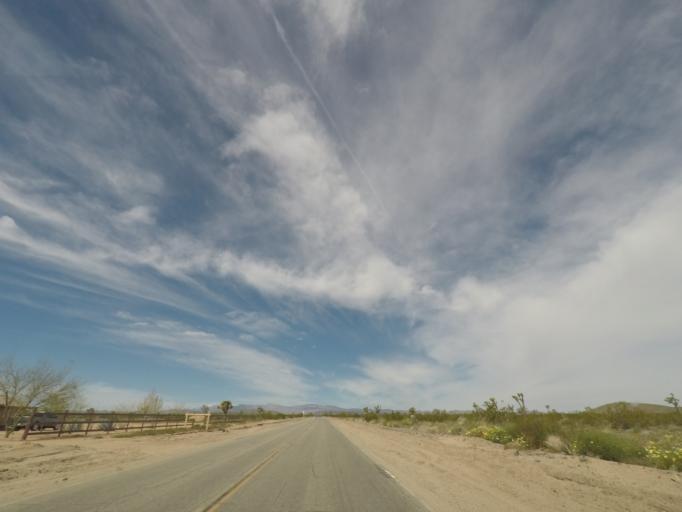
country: US
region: California
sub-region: San Bernardino County
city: Joshua Tree
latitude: 34.1929
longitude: -116.3411
